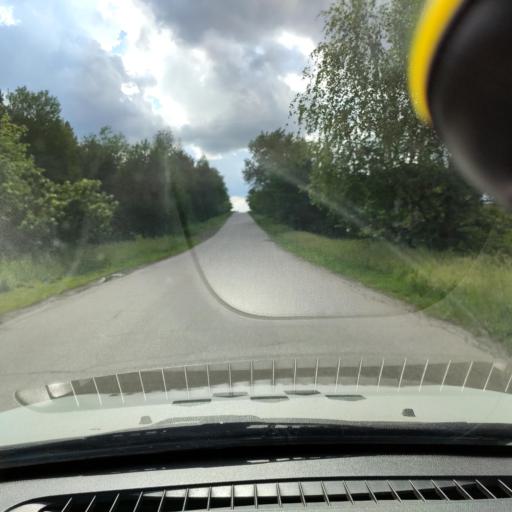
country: RU
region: Samara
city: Povolzhskiy
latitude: 53.6482
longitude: 49.7492
